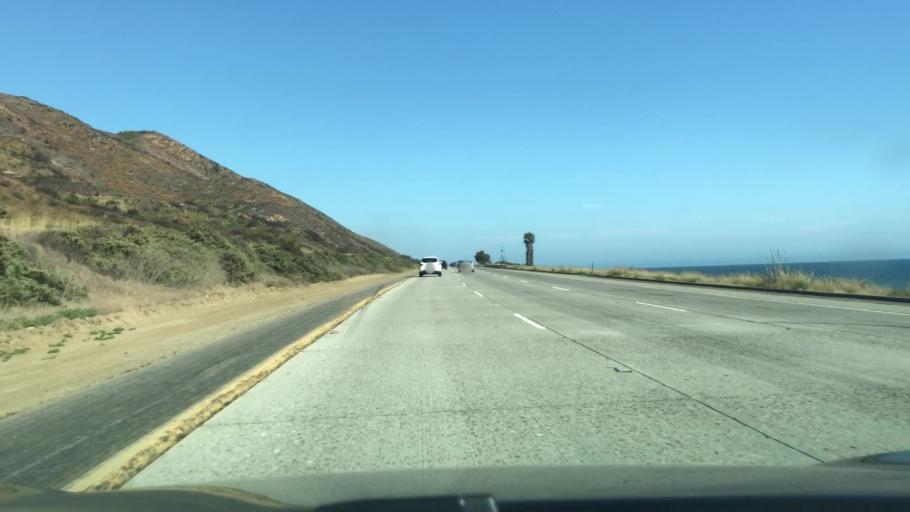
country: US
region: California
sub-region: Ventura County
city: Ventura
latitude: 34.3332
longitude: -119.4013
